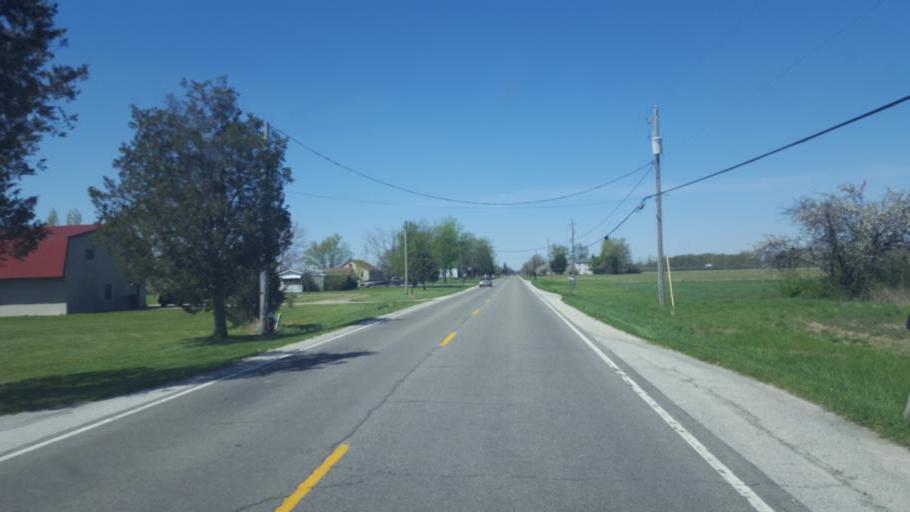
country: US
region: Ohio
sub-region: Ottawa County
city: Oak Harbor
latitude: 41.4864
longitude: -83.0802
